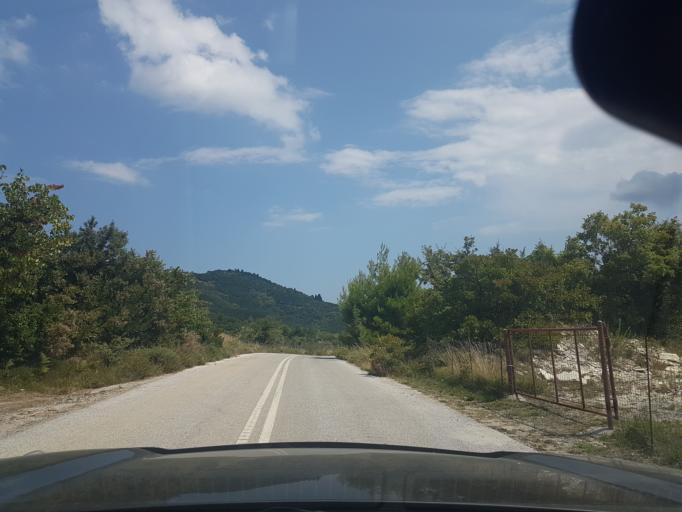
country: GR
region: Central Greece
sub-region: Nomos Evvoias
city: Kymi
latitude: 38.6477
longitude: 24.0434
